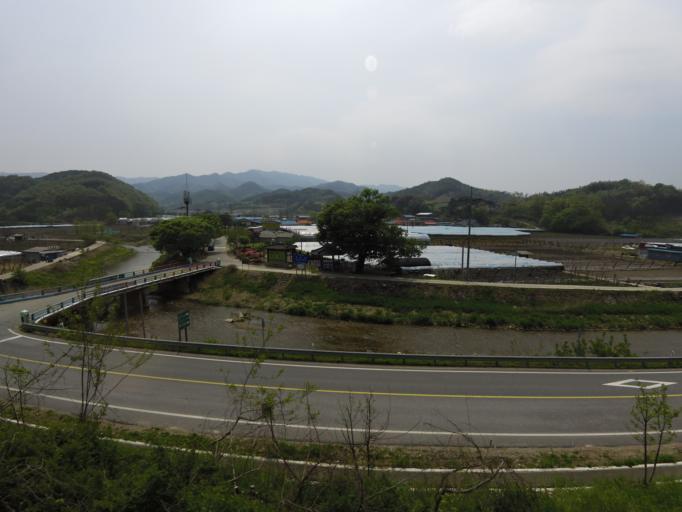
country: KR
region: Chungcheongbuk-do
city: Yong-dong
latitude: 36.1769
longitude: 127.8223
